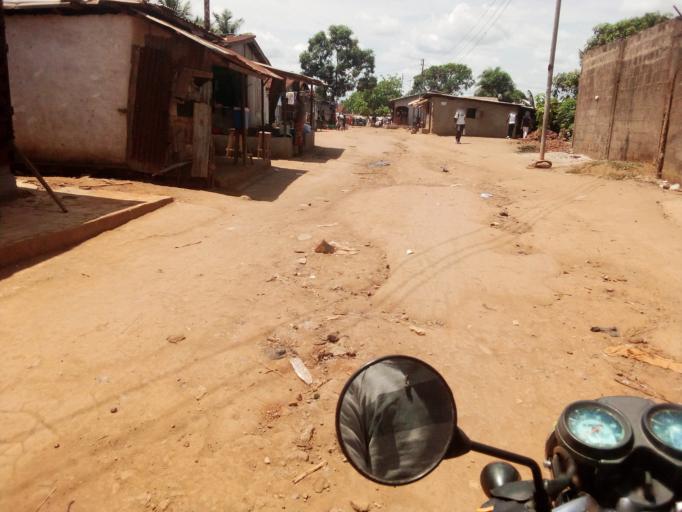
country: SL
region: Western Area
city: Waterloo
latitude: 8.3295
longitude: -13.0759
